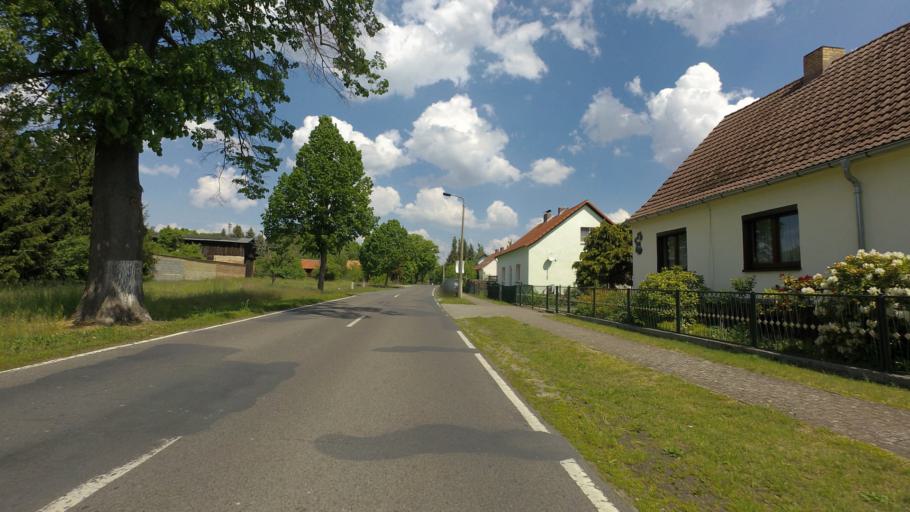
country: DE
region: Brandenburg
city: Straupitz
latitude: 51.9351
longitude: 14.1690
